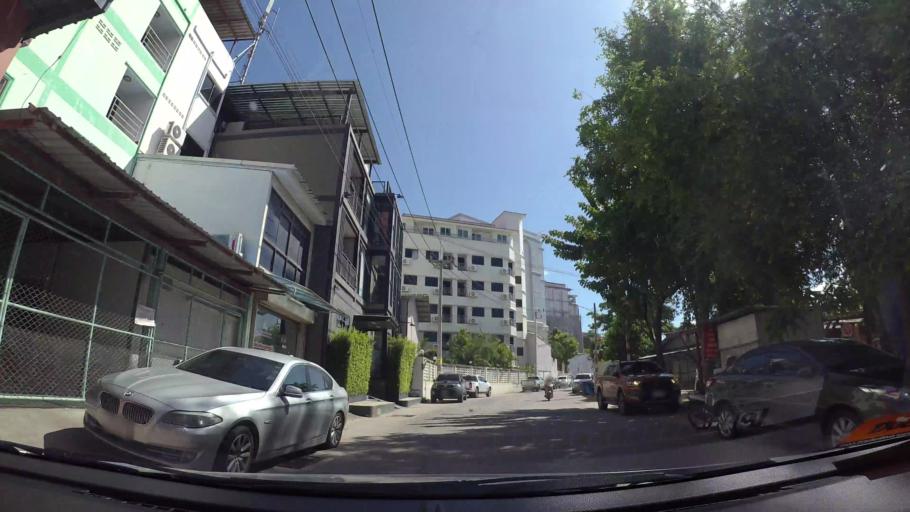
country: TH
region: Chon Buri
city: Phatthaya
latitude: 12.9469
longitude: 100.8968
